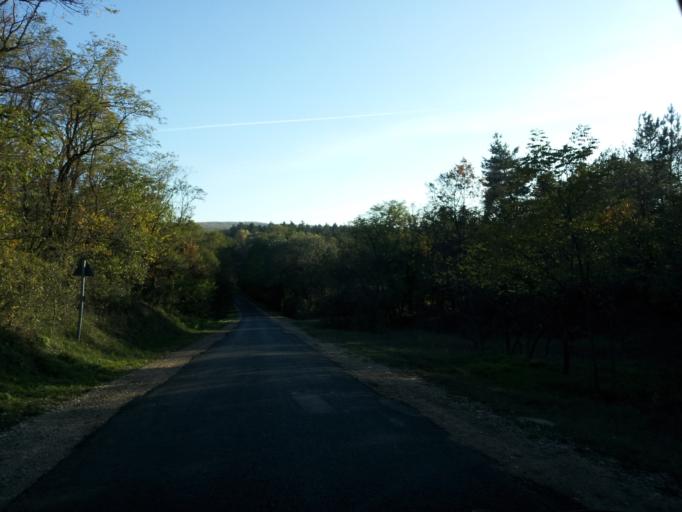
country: HU
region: Gyor-Moson-Sopron
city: Bakonyszentlaszlo
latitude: 47.3715
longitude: 17.8155
